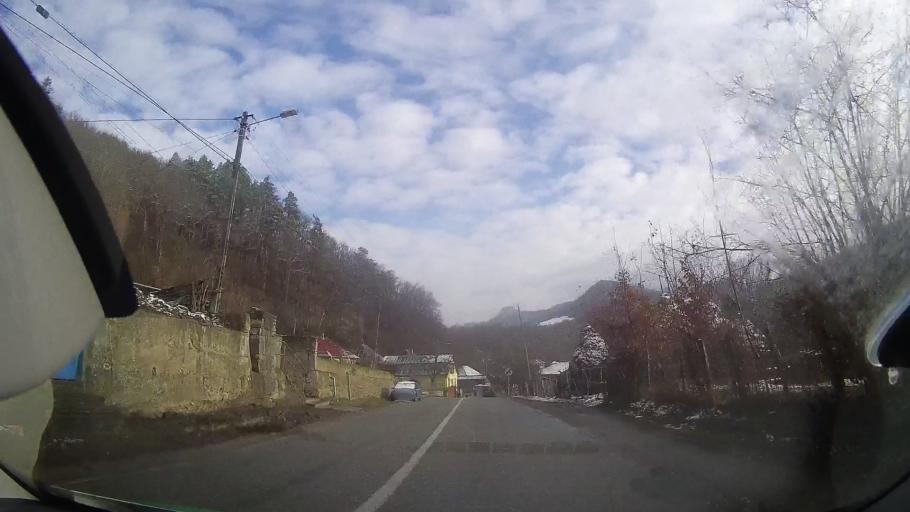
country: RO
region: Alba
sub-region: Oras Baia de Aries
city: Baia de Aries
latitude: 46.3824
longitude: 23.2726
